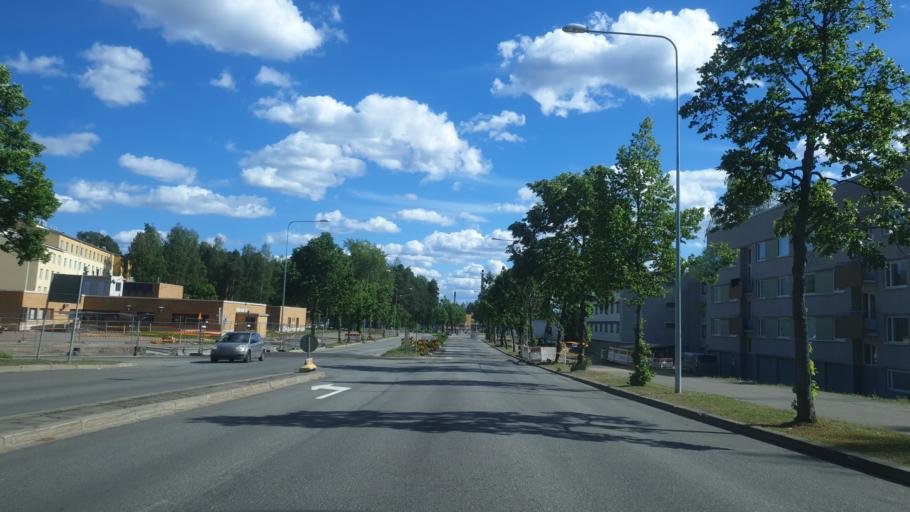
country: FI
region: Northern Savo
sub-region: Varkaus
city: Varkaus
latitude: 62.3304
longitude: 27.8873
